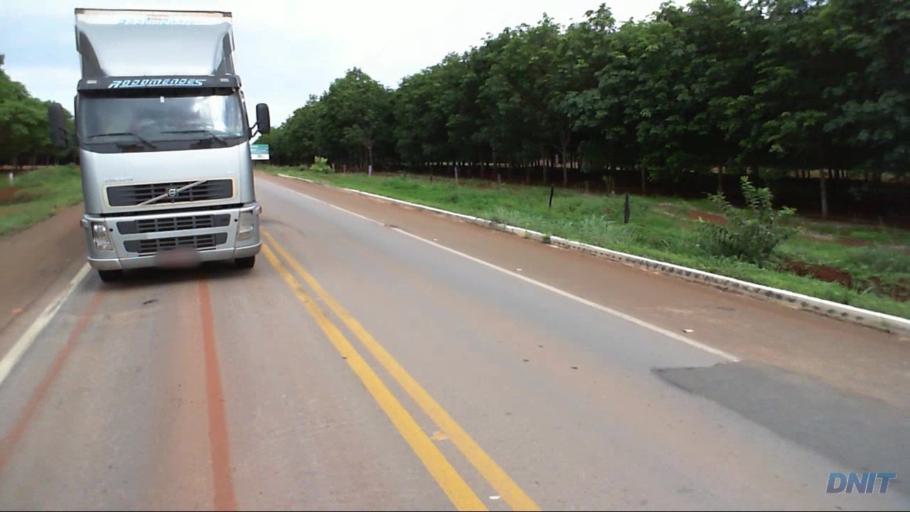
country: BR
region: Goias
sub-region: Barro Alto
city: Barro Alto
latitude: -14.8788
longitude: -48.9924
